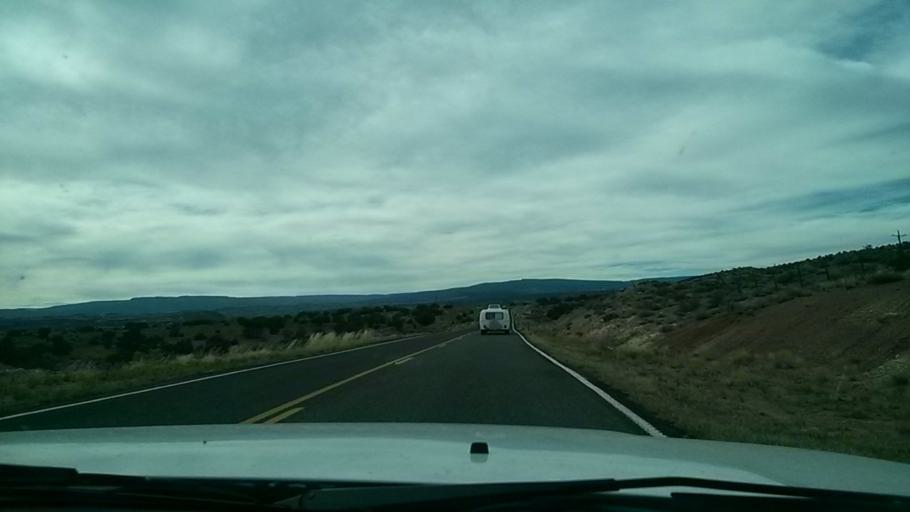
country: US
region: Utah
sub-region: Wayne County
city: Loa
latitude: 37.7428
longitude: -111.5590
